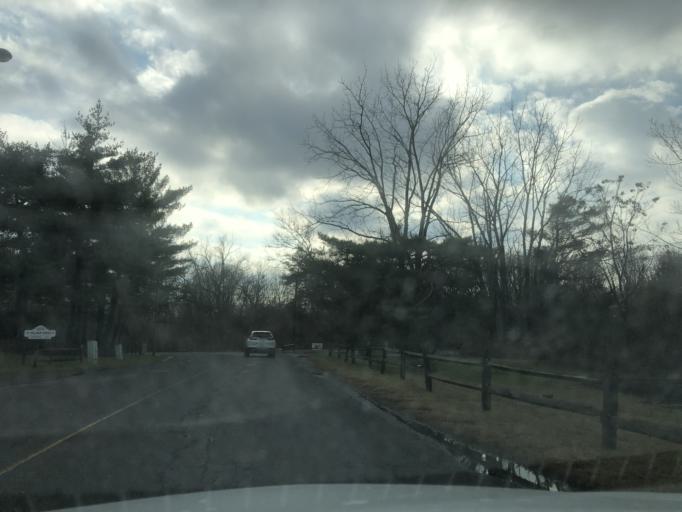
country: US
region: New Jersey
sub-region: Camden County
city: Glendora
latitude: 39.8263
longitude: -75.0790
